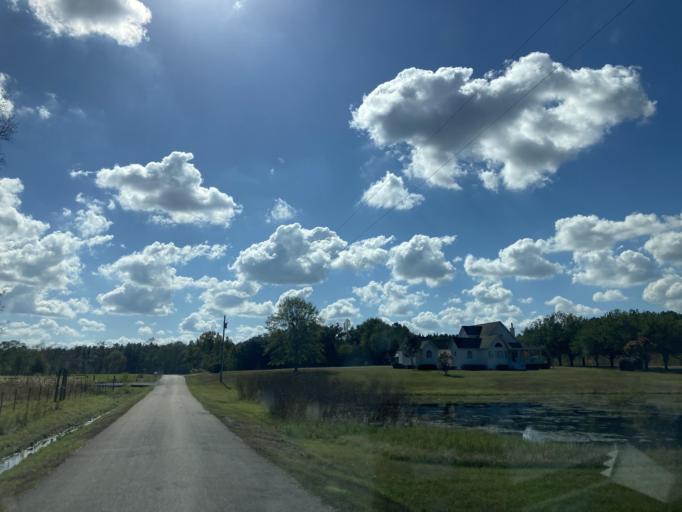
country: US
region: Mississippi
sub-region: Lamar County
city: West Hattiesburg
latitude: 31.2513
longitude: -89.4302
